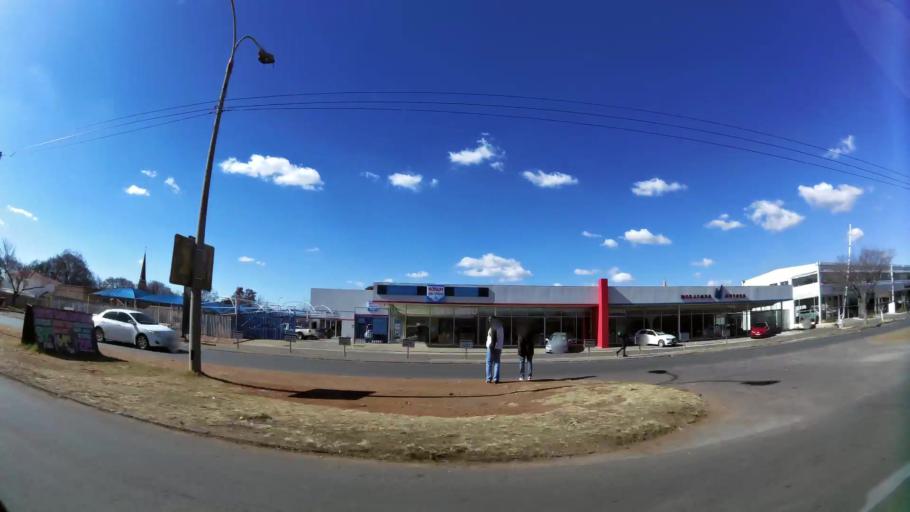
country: ZA
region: Gauteng
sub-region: West Rand District Municipality
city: Carletonville
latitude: -26.3546
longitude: 27.3991
